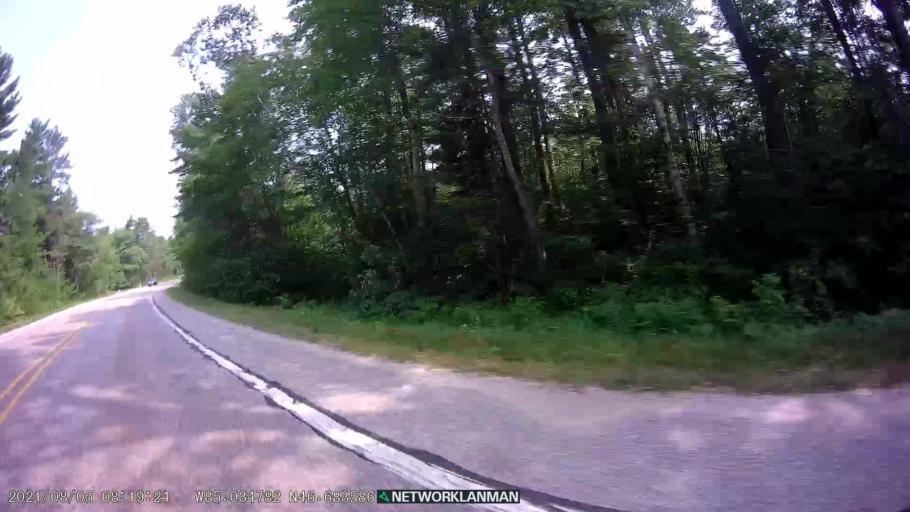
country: US
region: Michigan
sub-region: Luce County
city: Newberry
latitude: 46.6838
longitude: -85.0352
